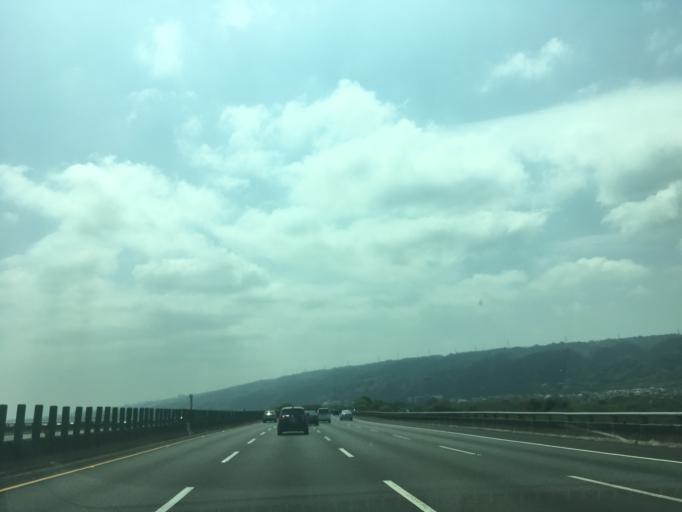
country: TW
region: Taiwan
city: Zhongxing New Village
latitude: 23.9832
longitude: 120.6526
